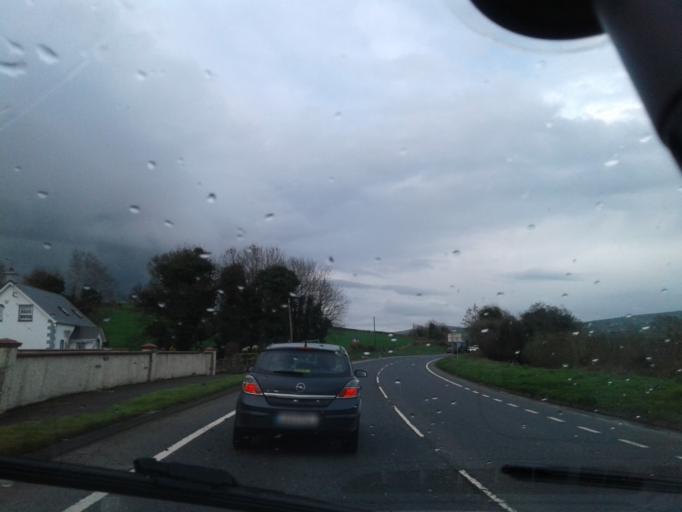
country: GB
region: Northern Ireland
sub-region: Strabane District
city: Sion Mills
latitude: 54.7684
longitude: -7.4688
